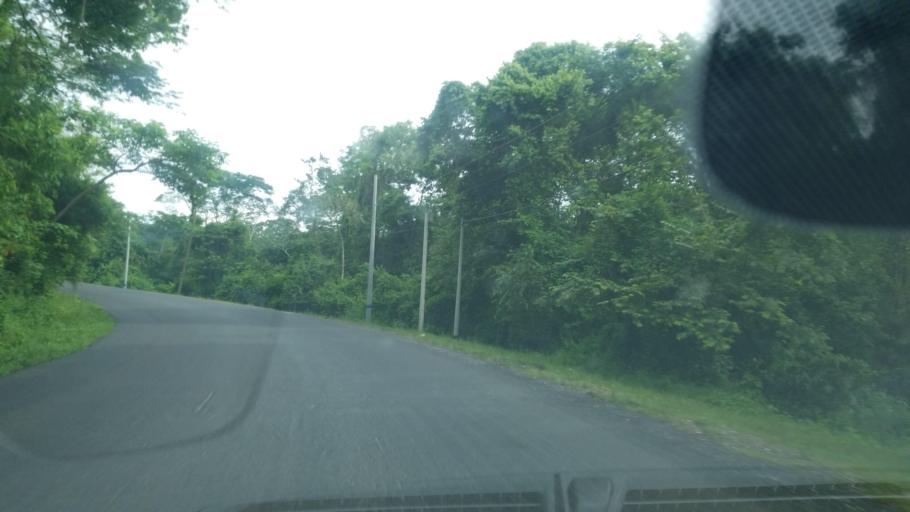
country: HN
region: Santa Barbara
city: Petoa
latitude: 15.2368
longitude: -88.2682
